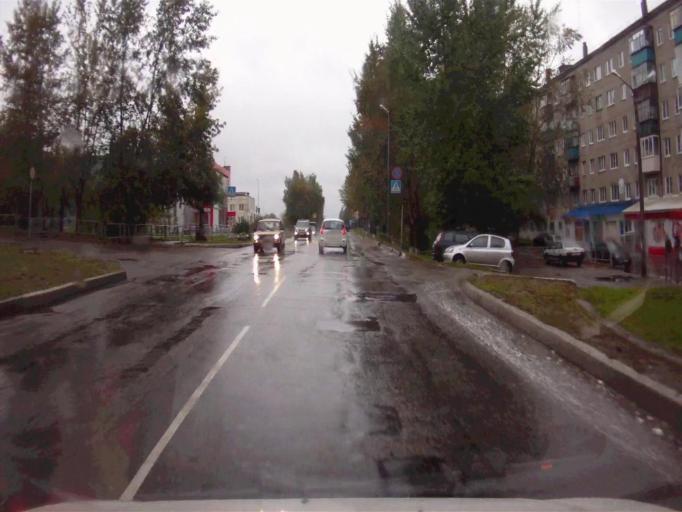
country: RU
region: Chelyabinsk
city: Kyshtym
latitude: 55.7033
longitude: 60.5561
